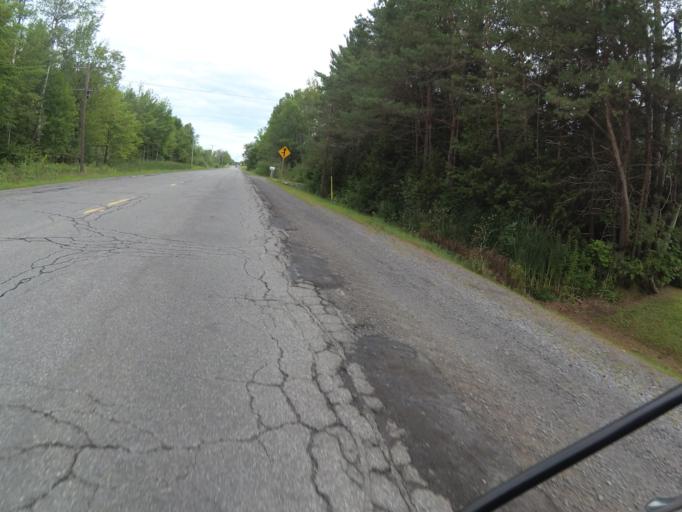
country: CA
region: Ontario
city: Bourget
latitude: 45.3624
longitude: -75.2626
